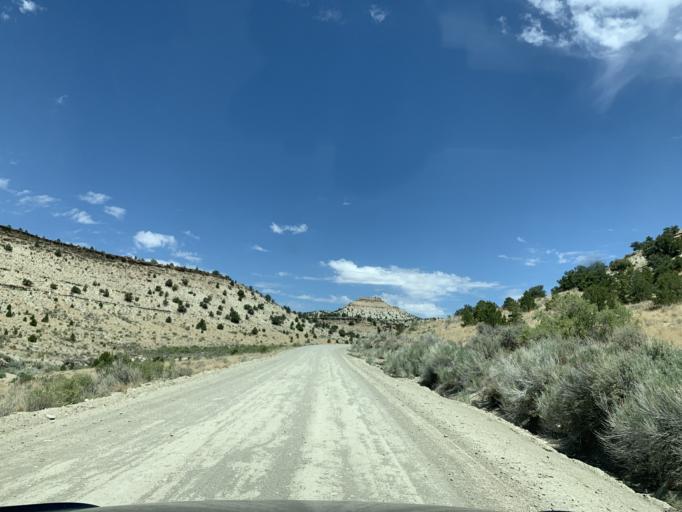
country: US
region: Utah
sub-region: Duchesne County
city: Duchesne
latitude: 39.8541
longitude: -110.2532
